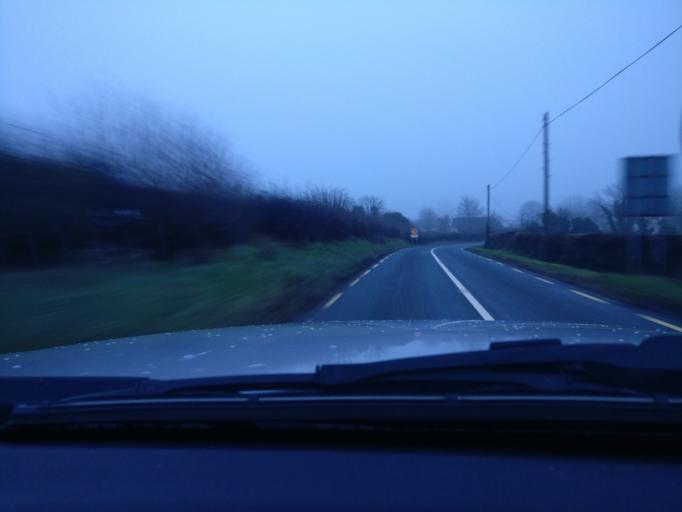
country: IE
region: Leinster
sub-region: An Mhi
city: Ballivor
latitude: 53.6093
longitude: -7.0170
